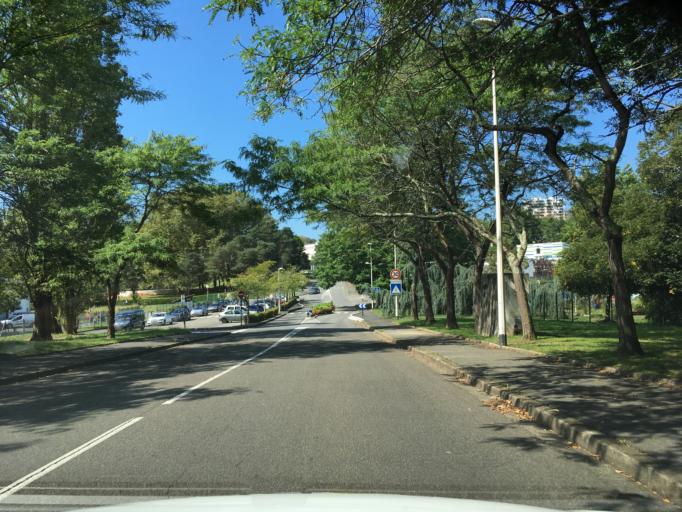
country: FR
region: Aquitaine
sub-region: Departement des Pyrenees-Atlantiques
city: Boucau
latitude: 43.4977
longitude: -1.4513
